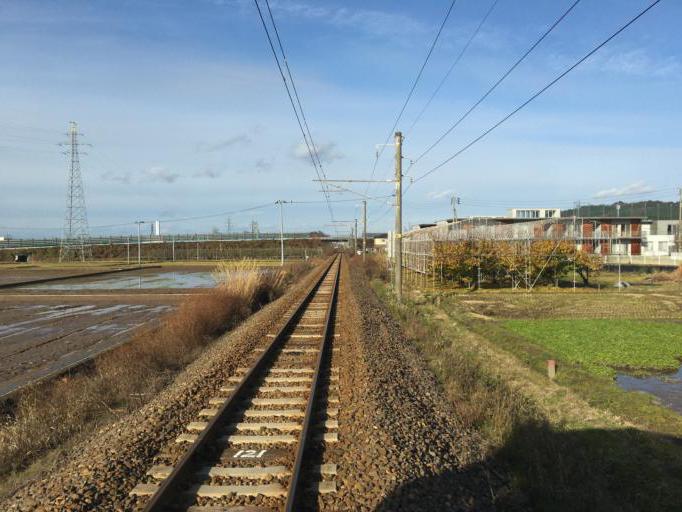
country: JP
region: Akita
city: Yuzawa
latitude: 39.1381
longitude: 140.4855
